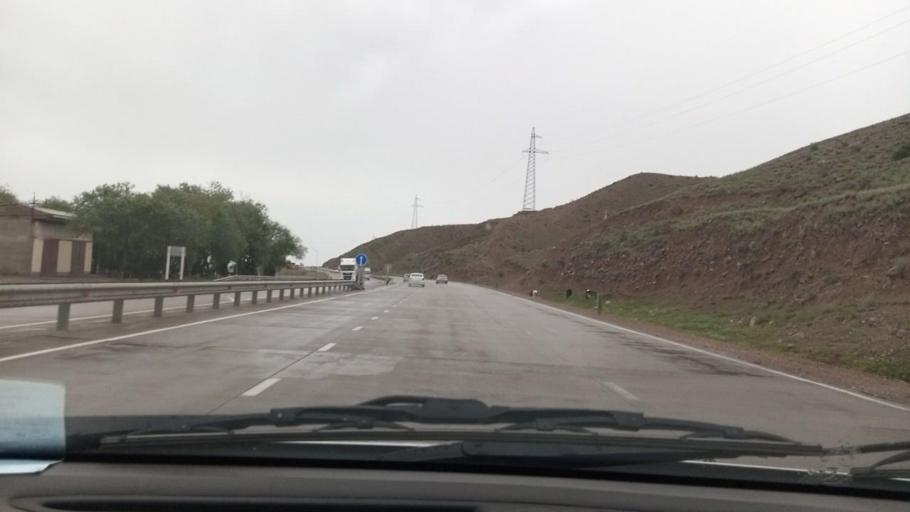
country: UZ
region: Namangan
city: Pop Shahri
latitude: 40.9474
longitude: 70.6817
